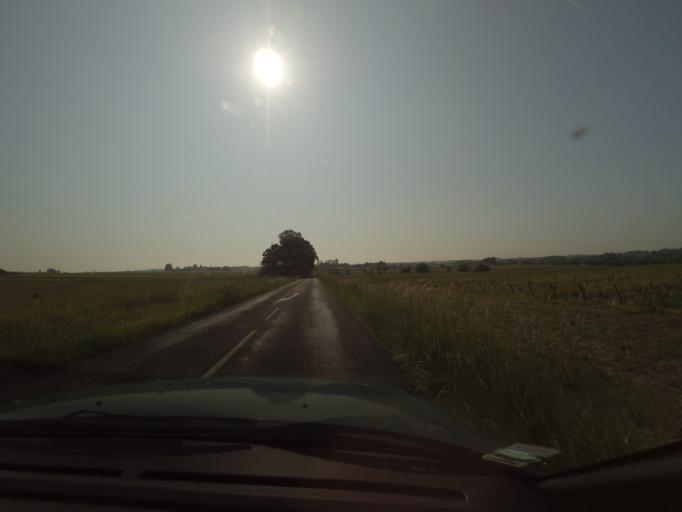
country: FR
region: Pays de la Loire
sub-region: Departement de la Loire-Atlantique
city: Mouzillon
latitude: 47.1457
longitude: -1.2964
